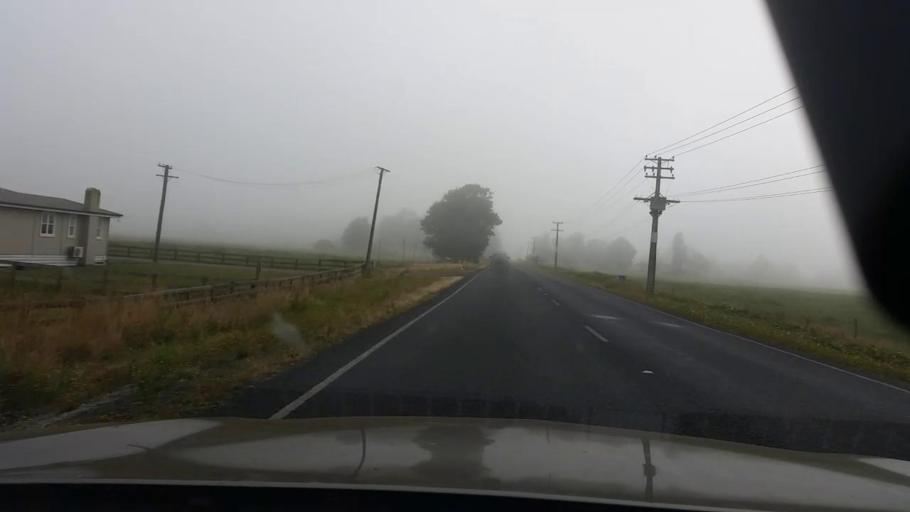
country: NZ
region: Waikato
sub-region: Hamilton City
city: Hamilton
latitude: -37.6334
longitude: 175.3065
